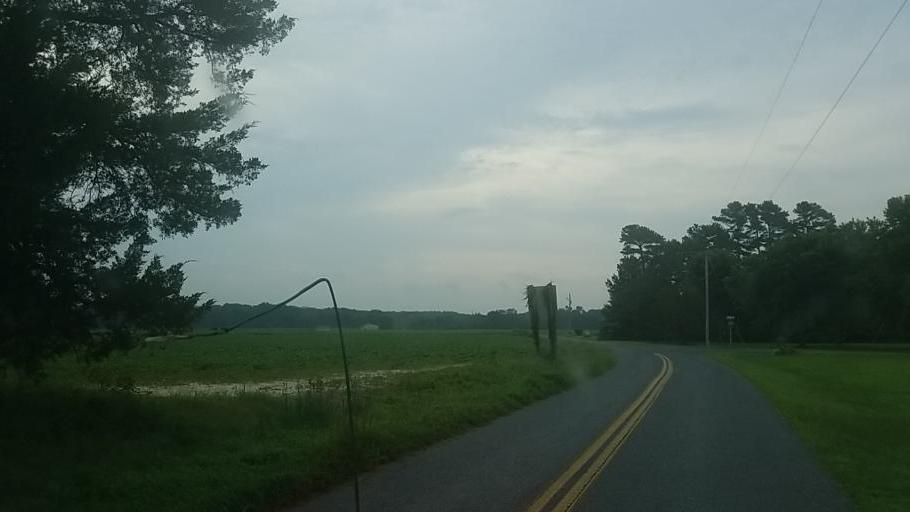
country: US
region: Delaware
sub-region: Sussex County
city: Selbyville
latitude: 38.4447
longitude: -75.2105
